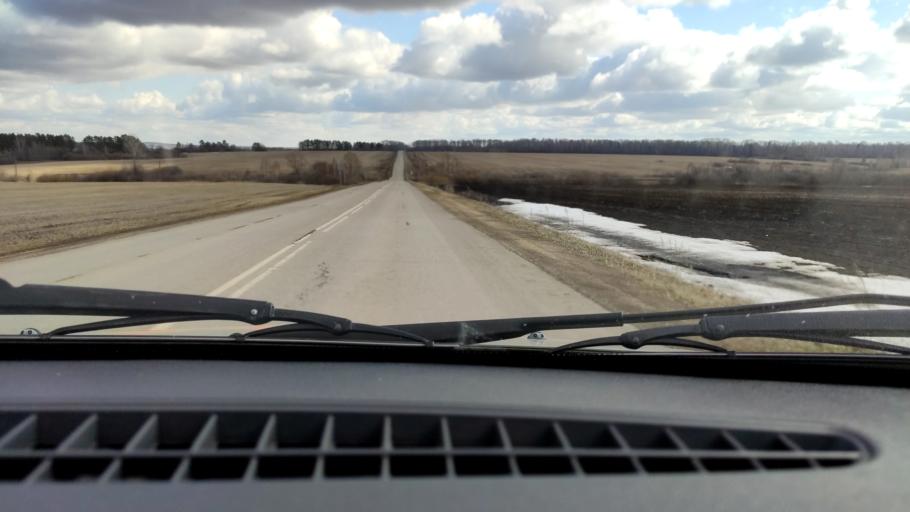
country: RU
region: Bashkortostan
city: Iglino
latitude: 54.8757
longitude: 56.5234
